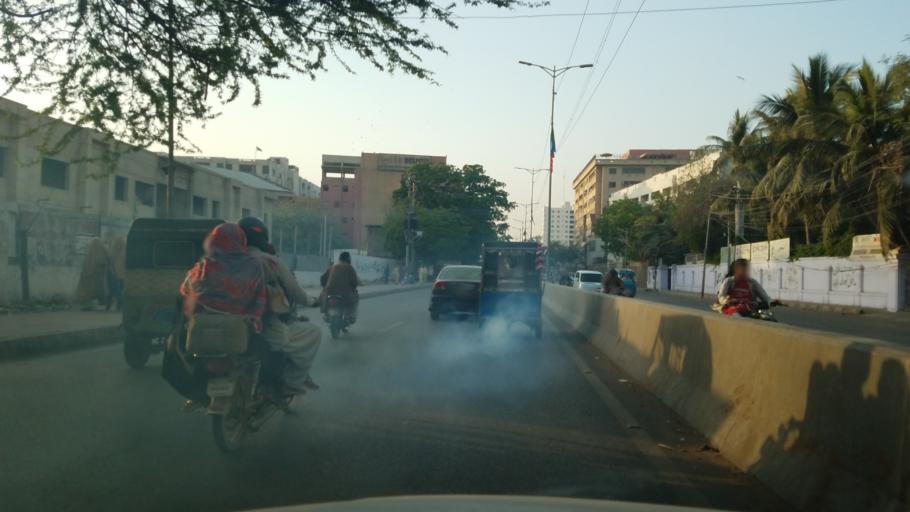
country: PK
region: Sindh
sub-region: Karachi District
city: Karachi
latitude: 24.8656
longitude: 67.0247
